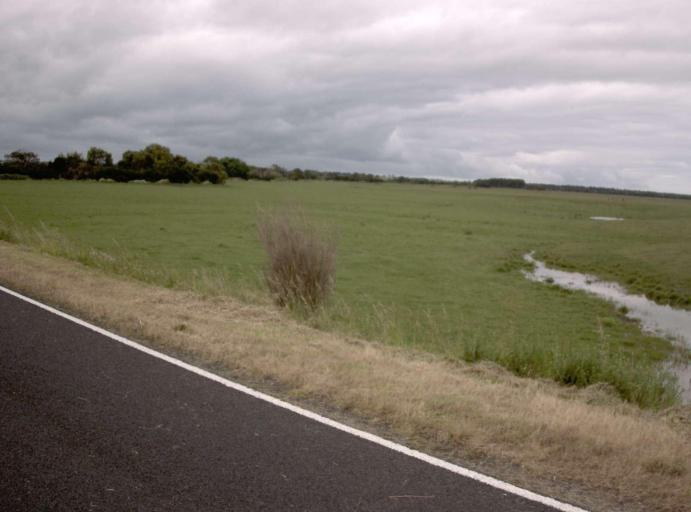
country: AU
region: Victoria
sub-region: Bass Coast
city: North Wonthaggi
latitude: -38.5714
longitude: 145.6312
